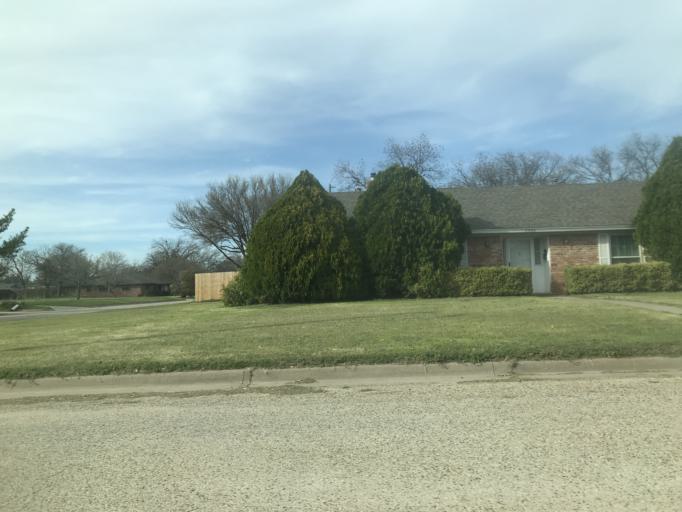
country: US
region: Texas
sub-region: Taylor County
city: Abilene
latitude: 32.4143
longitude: -99.7679
